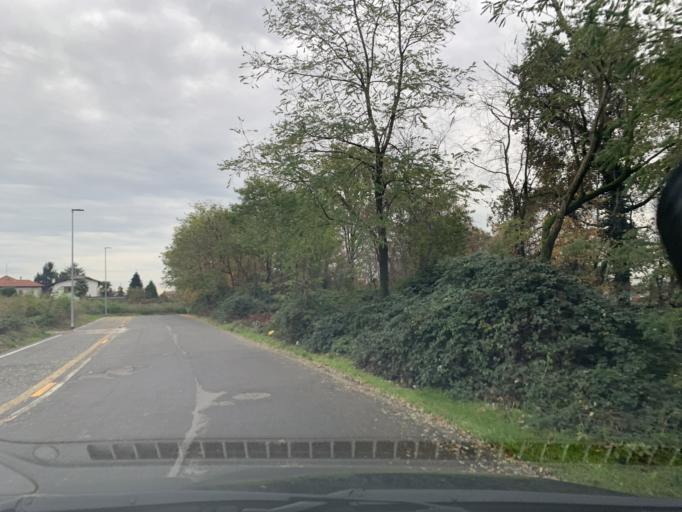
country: IT
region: Lombardy
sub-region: Provincia di Como
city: Puginate
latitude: 45.7109
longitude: 9.0539
